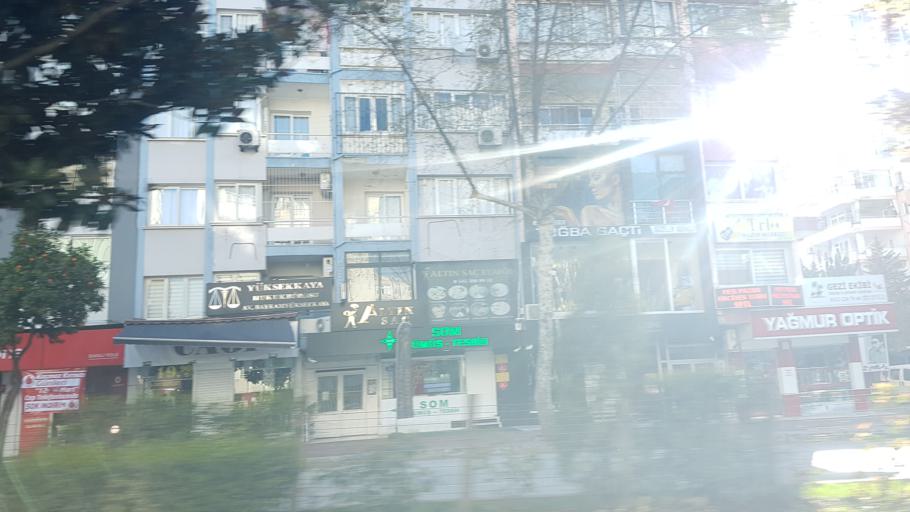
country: TR
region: Adana
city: Adana
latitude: 37.0252
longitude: 35.3145
